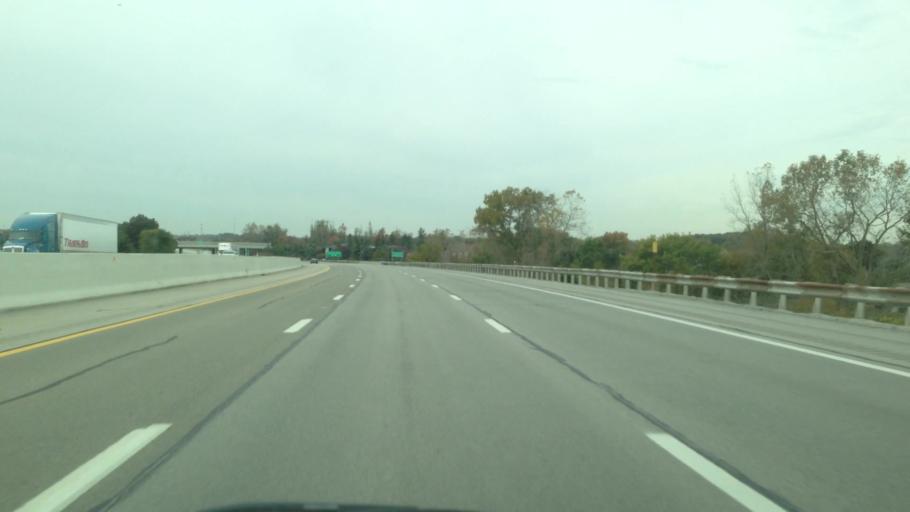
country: US
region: Ohio
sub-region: Lucas County
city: Maumee
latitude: 41.5900
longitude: -83.6382
